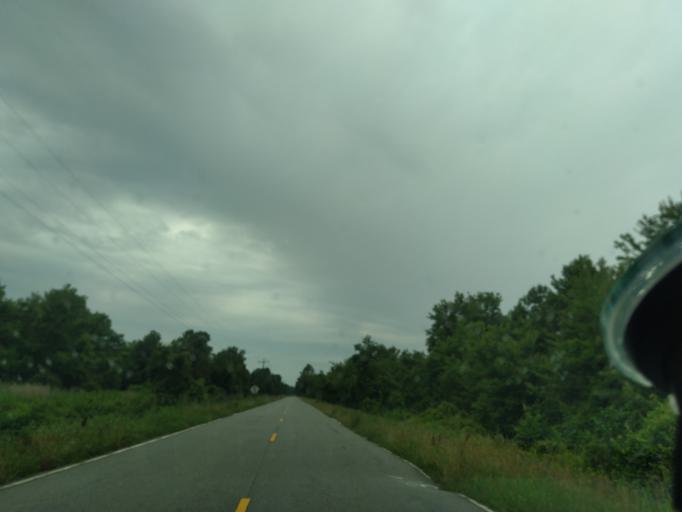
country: US
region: North Carolina
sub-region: Washington County
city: Plymouth
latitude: 35.8022
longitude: -76.5169
